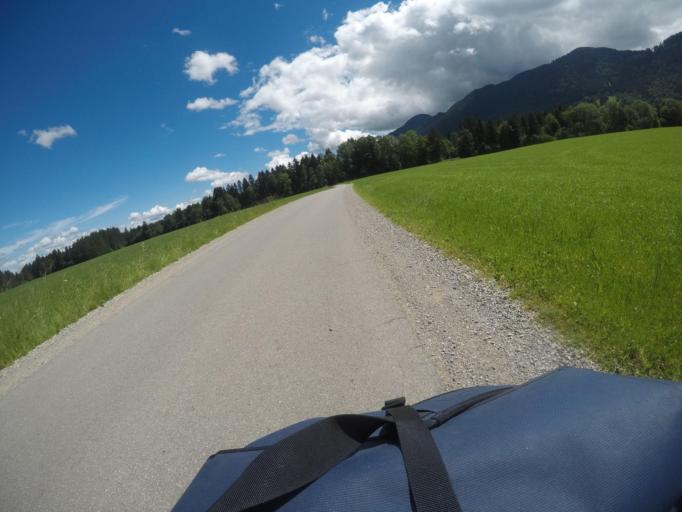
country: DE
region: Bavaria
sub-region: Swabia
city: Halblech
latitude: 47.6300
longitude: 10.8123
